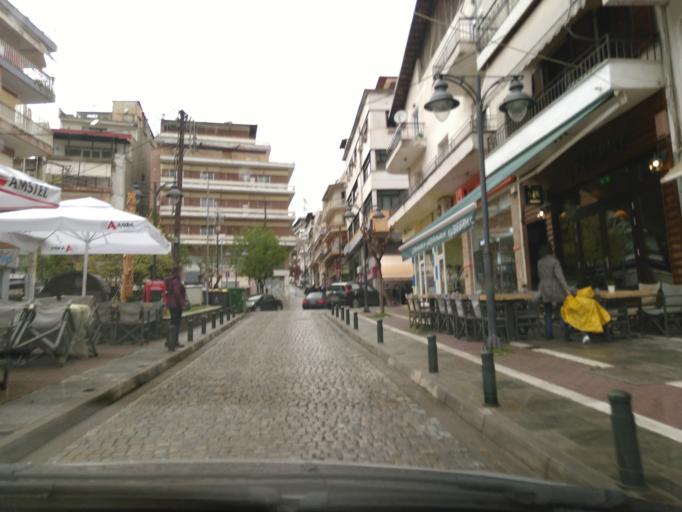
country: GR
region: West Macedonia
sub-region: Nomos Grevenon
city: Grevena
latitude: 40.0846
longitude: 21.4295
